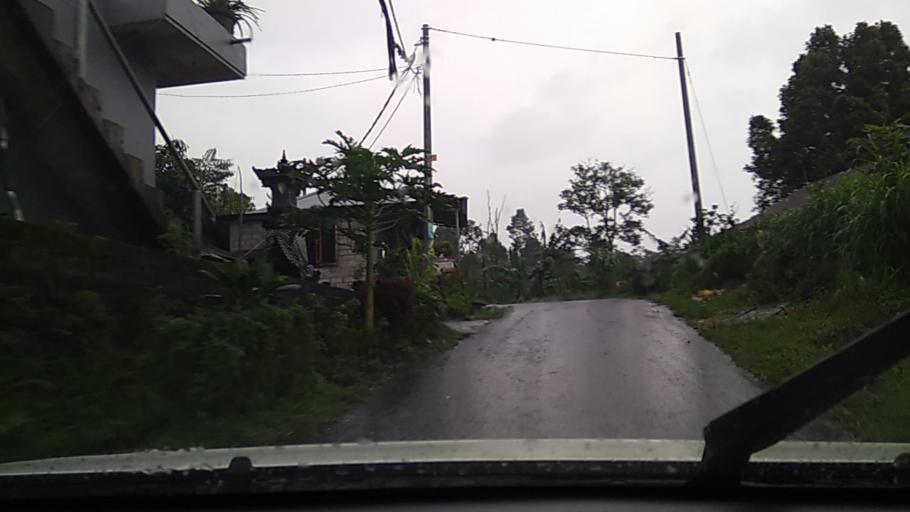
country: ID
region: Bali
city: Banjar Ambengan
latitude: -8.2187
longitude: 115.1676
